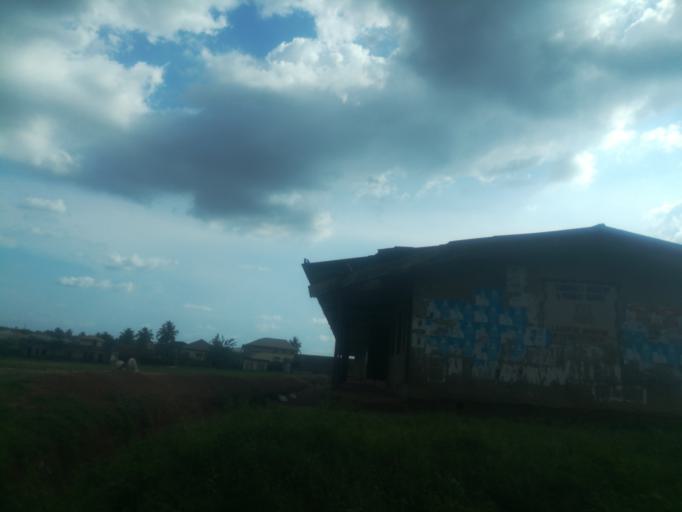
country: NG
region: Oyo
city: Ibadan
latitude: 7.4015
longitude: 3.8375
